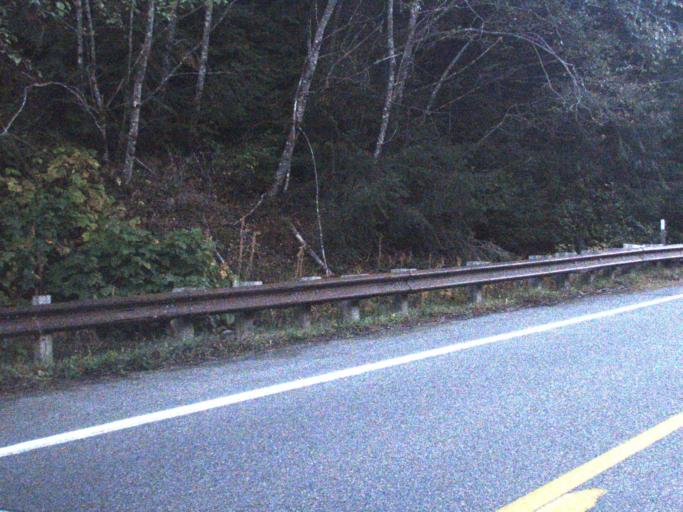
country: US
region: Washington
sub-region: Snohomish County
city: Darrington
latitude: 48.7068
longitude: -120.9752
